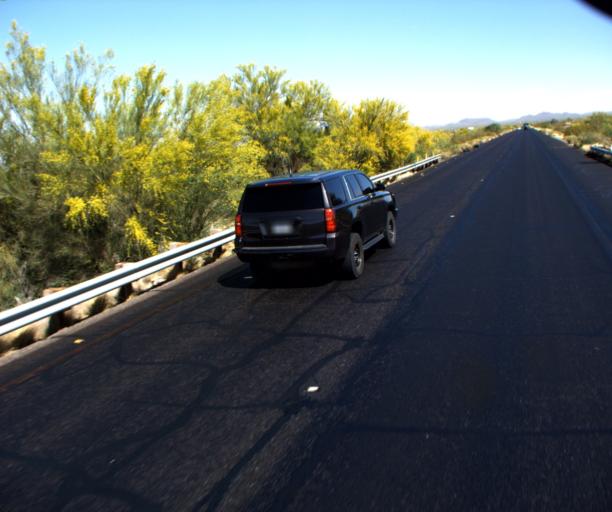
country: US
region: Arizona
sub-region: Pinal County
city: Maricopa
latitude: 32.8460
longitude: -112.2899
